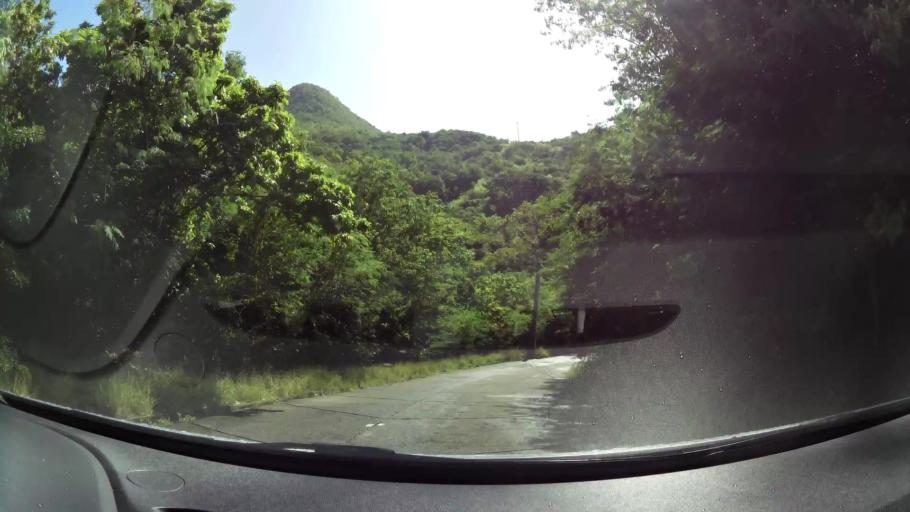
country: MQ
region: Martinique
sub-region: Martinique
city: Les Trois-Ilets
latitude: 14.4801
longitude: -61.0772
